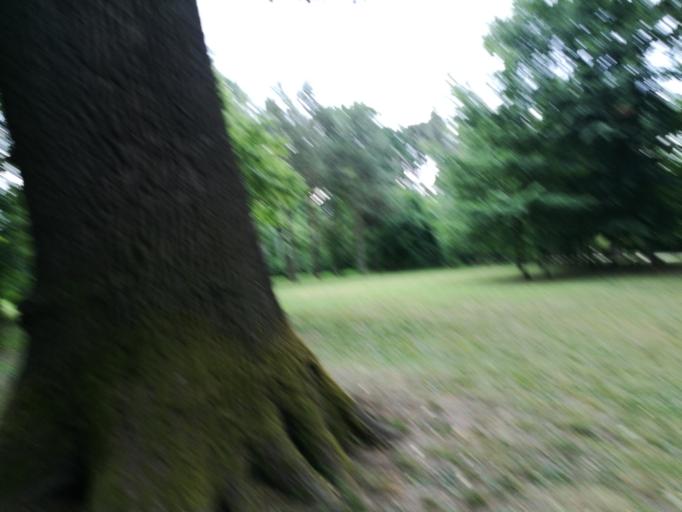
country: RO
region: Ilfov
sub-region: Comuna Mogosoaia
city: Mogosoaia
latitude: 44.5262
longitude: 25.9928
